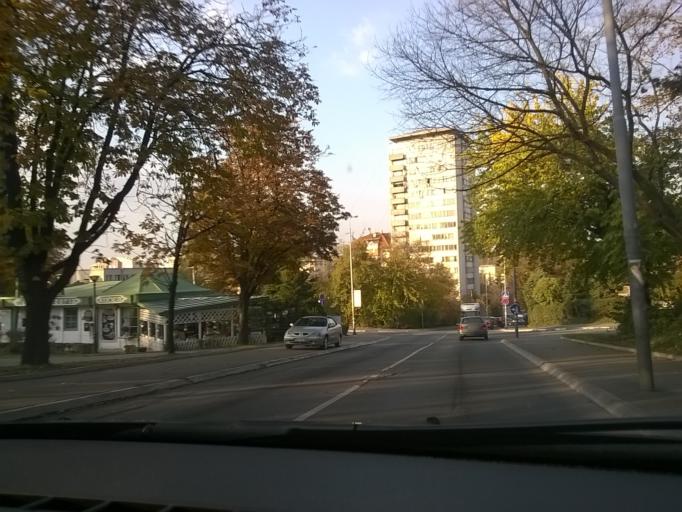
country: RS
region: Central Serbia
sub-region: Belgrade
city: Palilula
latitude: 44.7981
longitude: 20.4995
